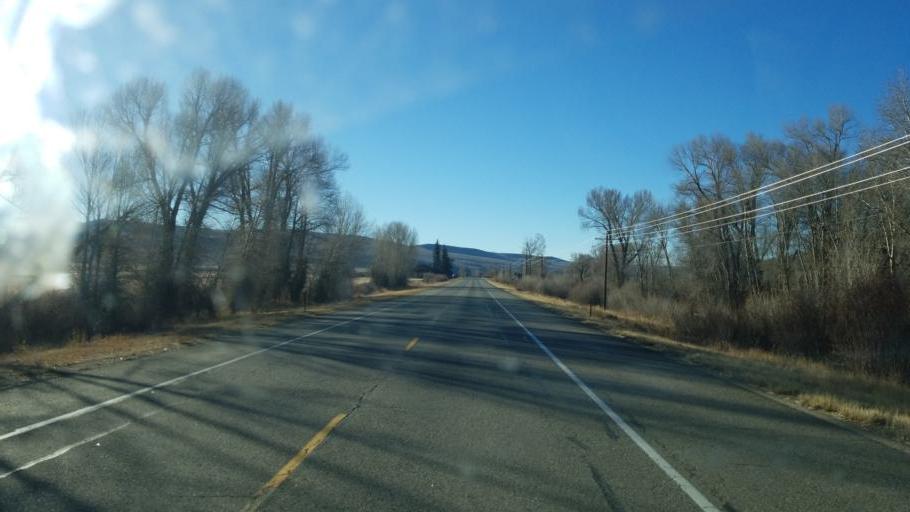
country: US
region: Colorado
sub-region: Gunnison County
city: Crested Butte
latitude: 38.7492
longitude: -106.8591
